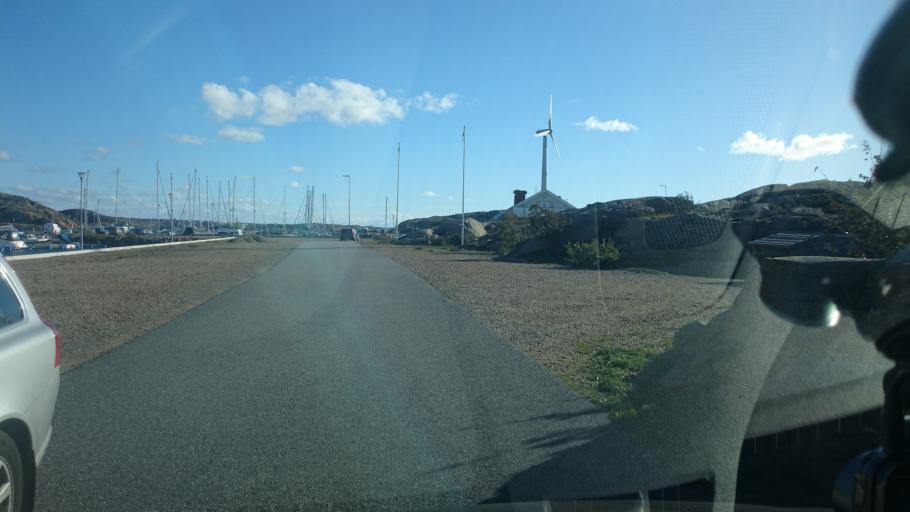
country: SE
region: Vaestra Goetaland
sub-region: Lysekils Kommun
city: Lysekil
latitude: 58.3165
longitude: 11.3950
